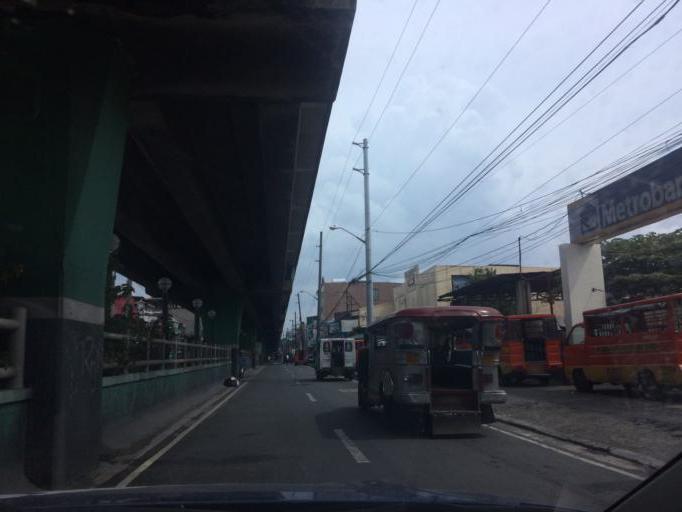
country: PH
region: Metro Manila
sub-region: Makati City
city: Makati City
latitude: 14.5523
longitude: 120.9976
